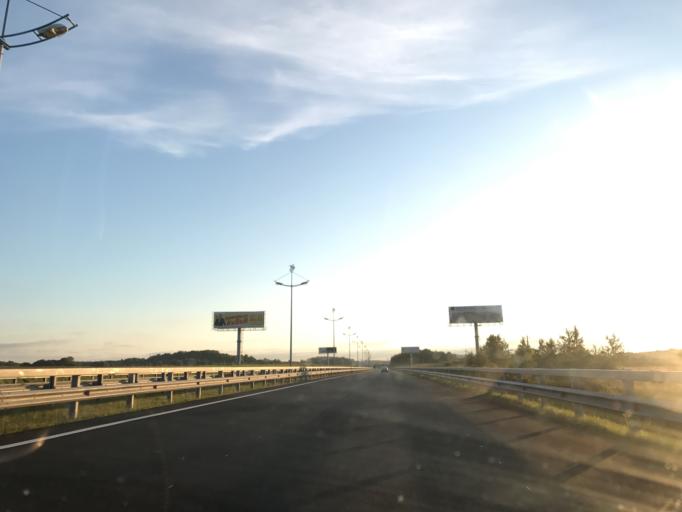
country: RU
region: Kaliningrad
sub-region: Gorod Kaliningrad
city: Pionerskiy
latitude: 54.9217
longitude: 20.3136
